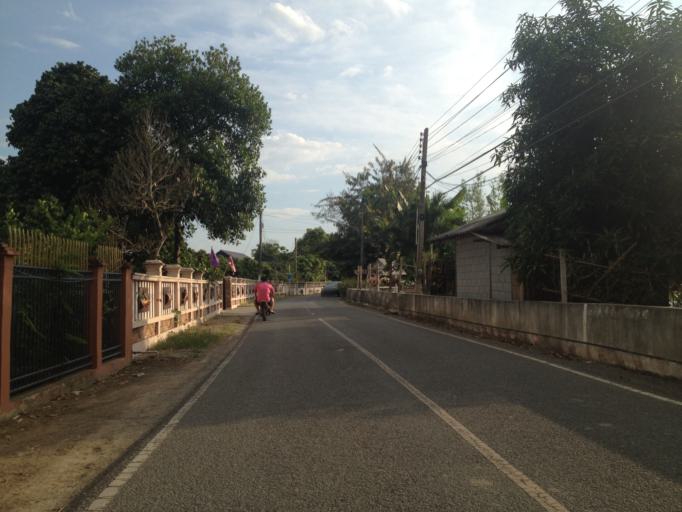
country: TH
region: Chiang Mai
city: Saraphi
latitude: 18.6982
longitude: 98.9871
